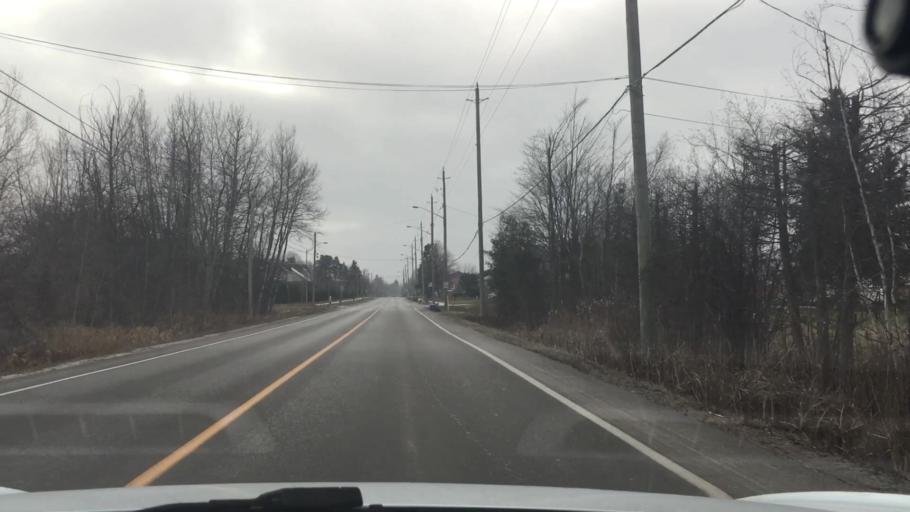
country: CA
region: Ontario
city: Oshawa
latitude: 43.9238
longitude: -78.7942
